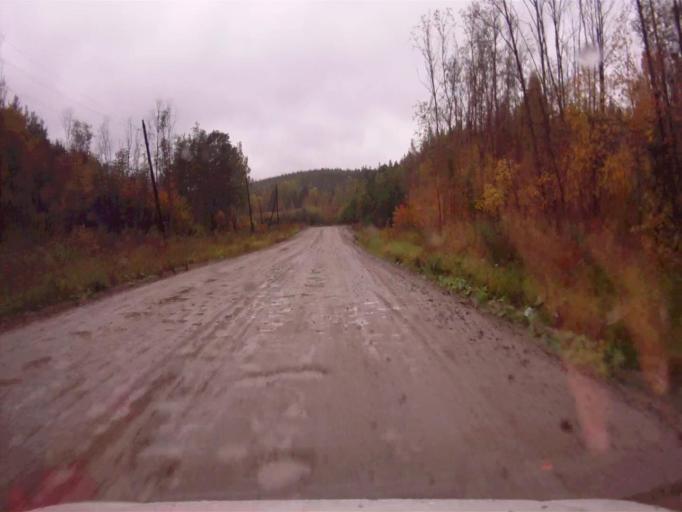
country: RU
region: Chelyabinsk
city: Kyshtym
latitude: 55.7408
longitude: 60.5090
